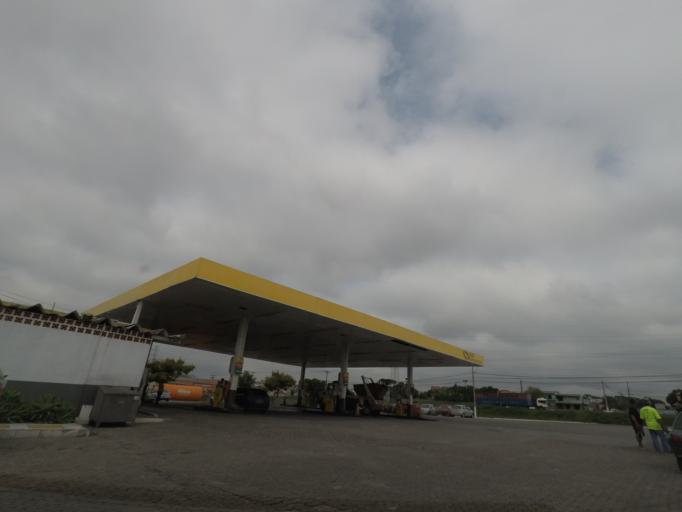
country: BR
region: Parana
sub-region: Curitiba
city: Curitiba
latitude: -25.4954
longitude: -49.3420
